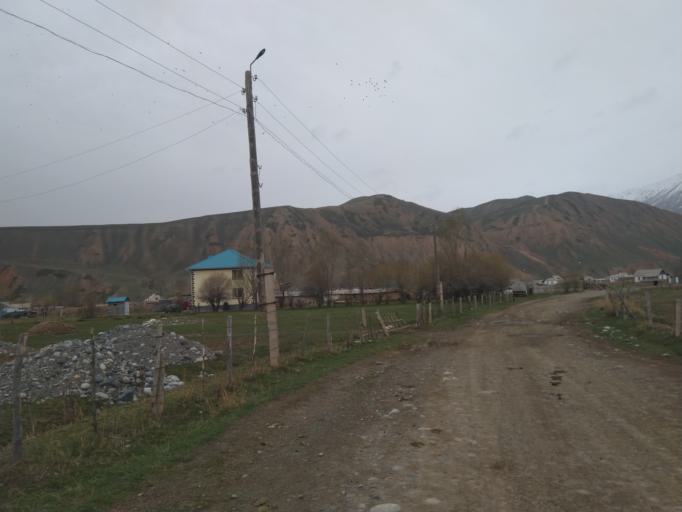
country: KG
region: Naryn
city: Naryn
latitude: 41.5152
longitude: 76.4398
